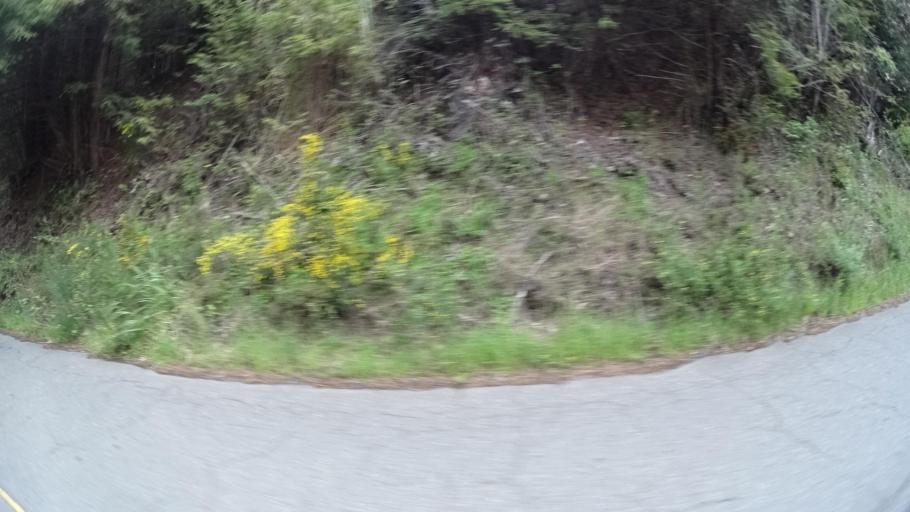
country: US
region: California
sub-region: Humboldt County
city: Blue Lake
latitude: 40.8735
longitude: -123.9760
